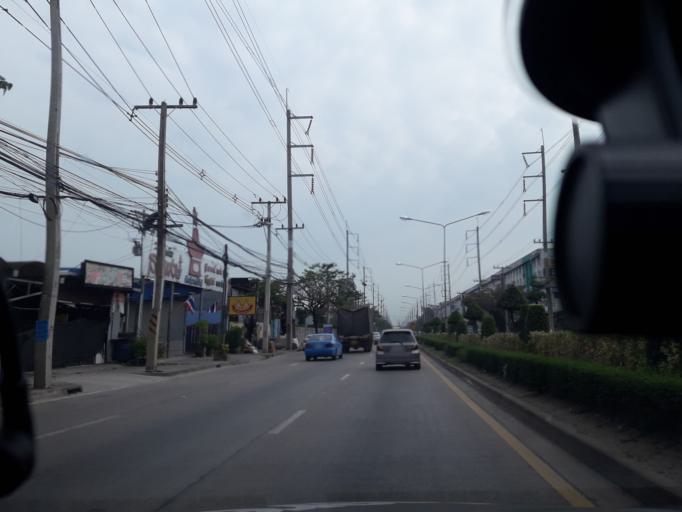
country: TH
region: Pathum Thani
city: Lam Luk Ka
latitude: 13.9342
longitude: 100.7269
